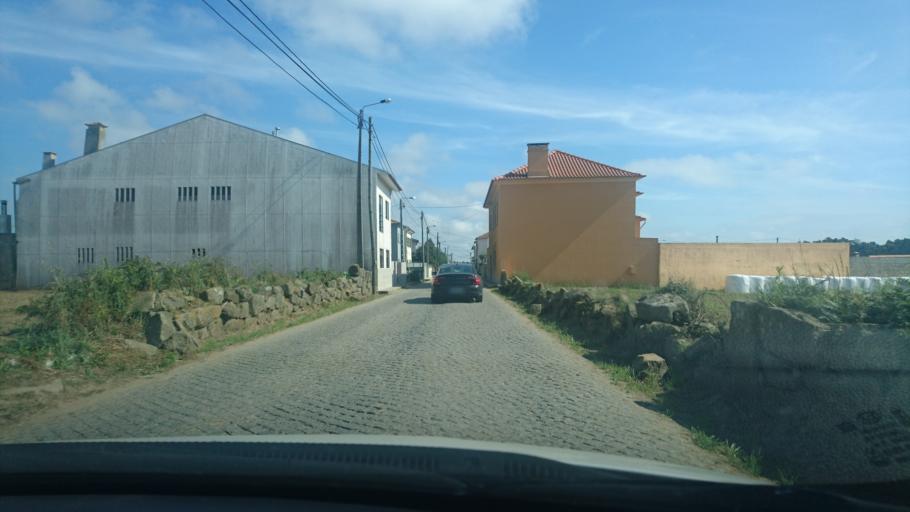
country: PT
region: Porto
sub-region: Matosinhos
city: Lavra
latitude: 41.2646
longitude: -8.7083
